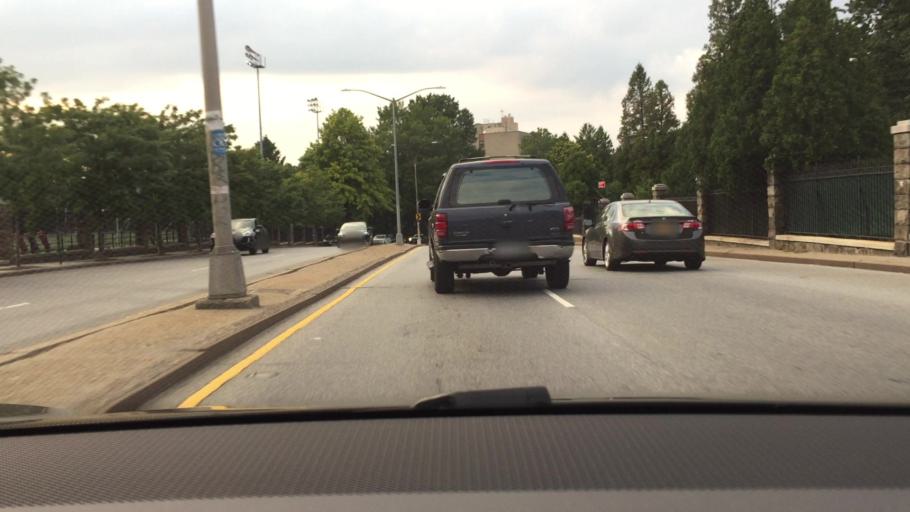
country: US
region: New York
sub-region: Bronx
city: The Bronx
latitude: 40.8636
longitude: -73.8832
